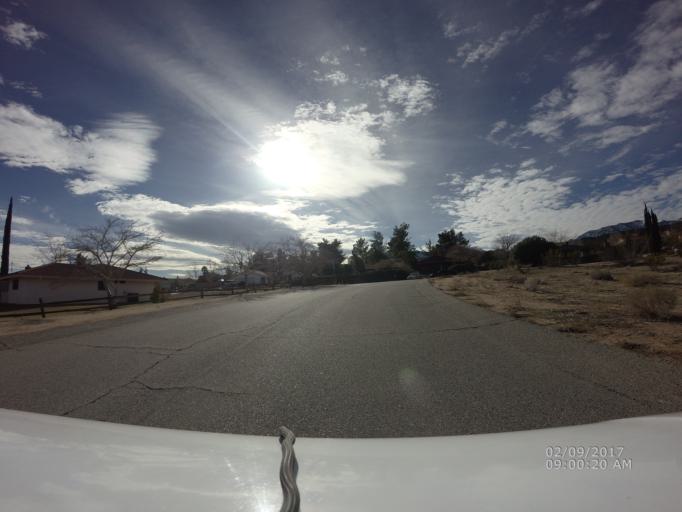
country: US
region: California
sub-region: Los Angeles County
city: Lake Los Angeles
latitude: 34.4739
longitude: -117.8399
